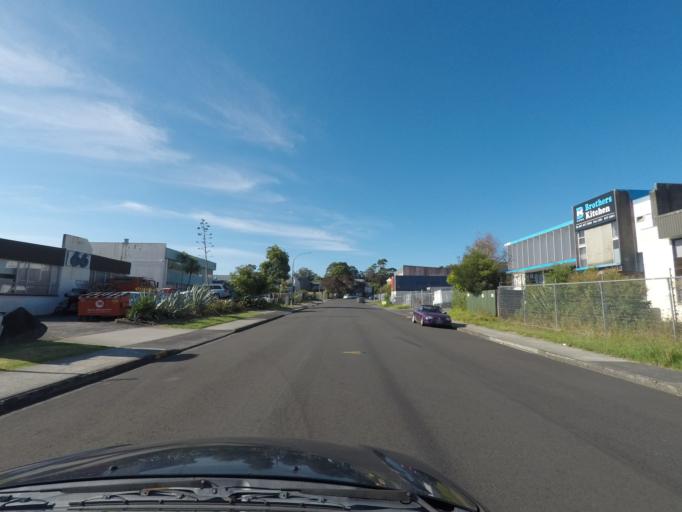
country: NZ
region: Auckland
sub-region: Auckland
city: Rosebank
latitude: -36.9053
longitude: 174.6980
